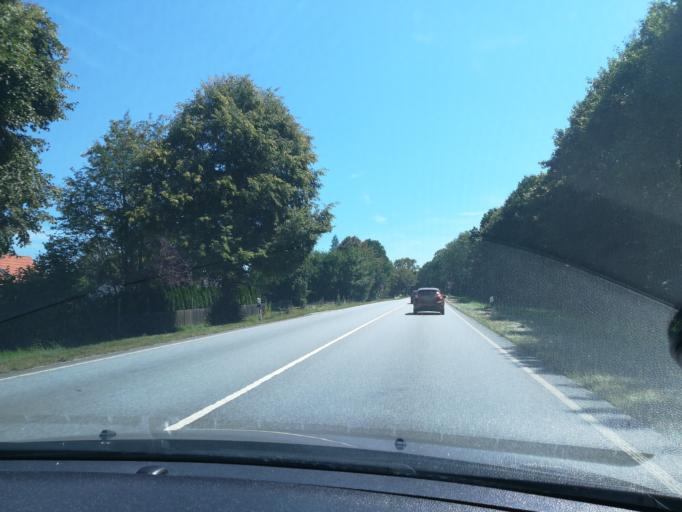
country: DE
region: Bavaria
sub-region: Upper Bavaria
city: Forstern
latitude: 48.1611
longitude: 11.9484
